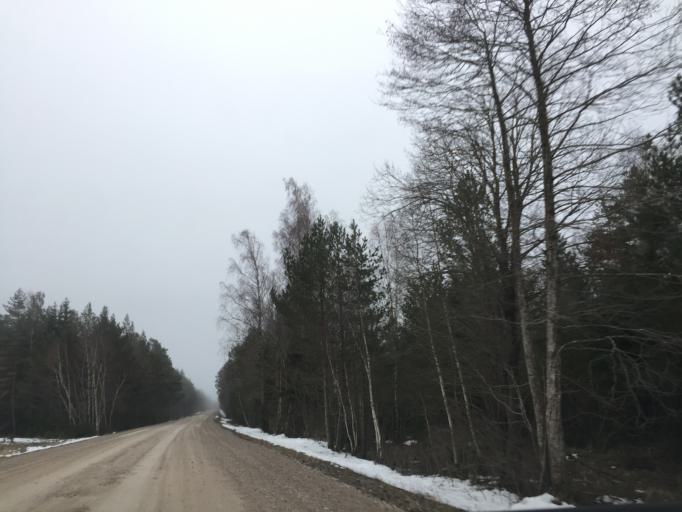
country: EE
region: Saare
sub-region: Kuressaare linn
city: Kuressaare
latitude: 58.4838
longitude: 21.9971
